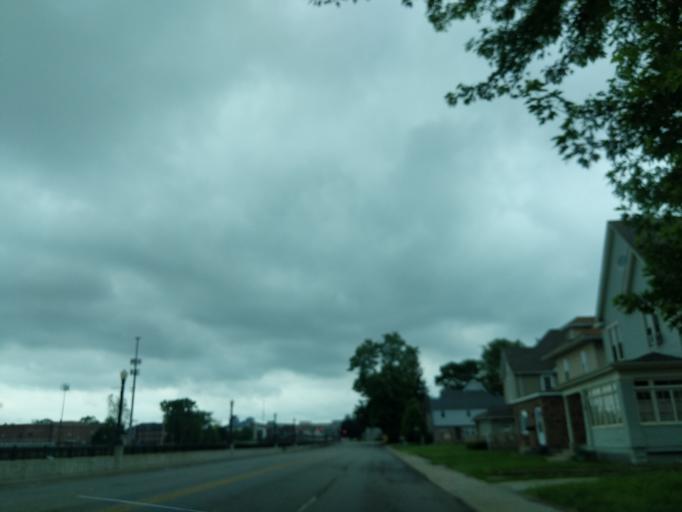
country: US
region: Indiana
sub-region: Delaware County
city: Muncie
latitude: 40.1999
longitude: -85.3916
